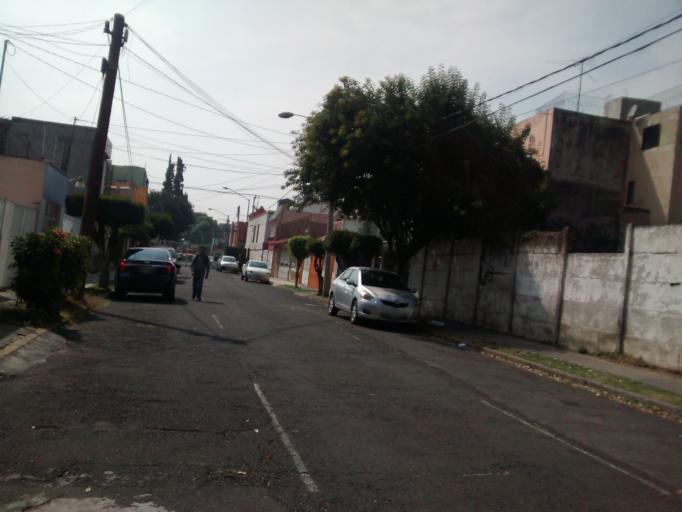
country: MX
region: Mexico
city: Colonia Lindavista
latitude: 19.4949
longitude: -99.1395
